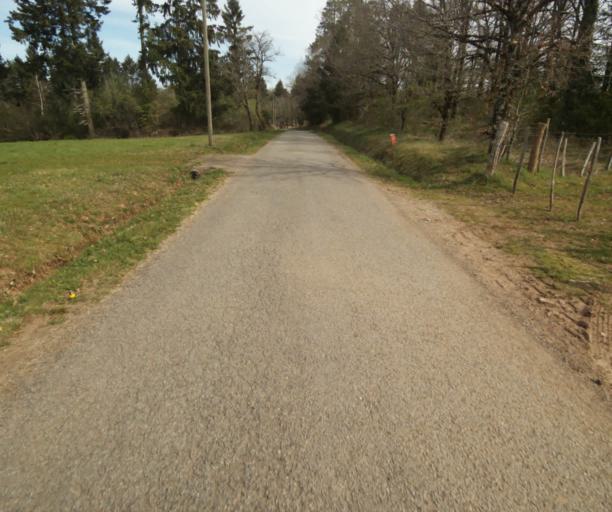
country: FR
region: Limousin
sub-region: Departement de la Correze
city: Correze
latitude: 45.3800
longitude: 1.8214
